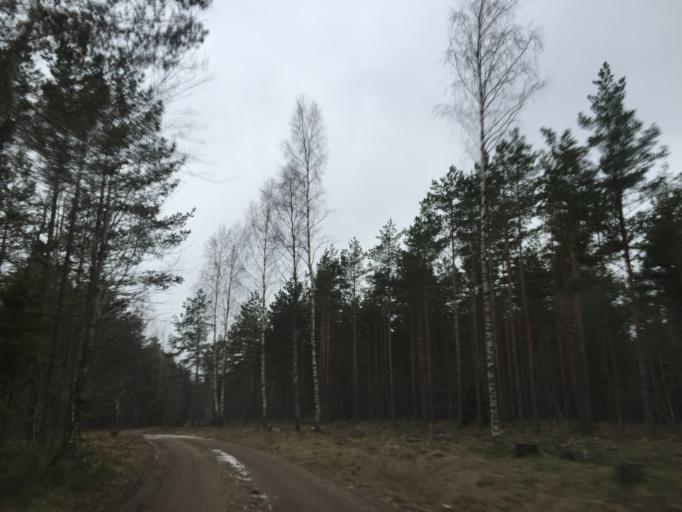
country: EE
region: Saare
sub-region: Kuressaare linn
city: Kuressaare
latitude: 58.3876
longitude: 22.2561
